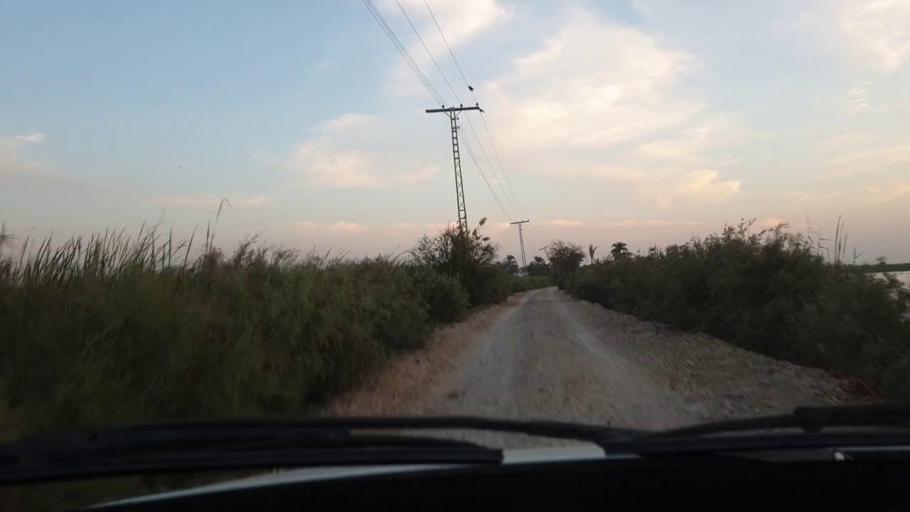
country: PK
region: Sindh
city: Tando Muhammad Khan
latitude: 25.0937
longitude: 68.3921
